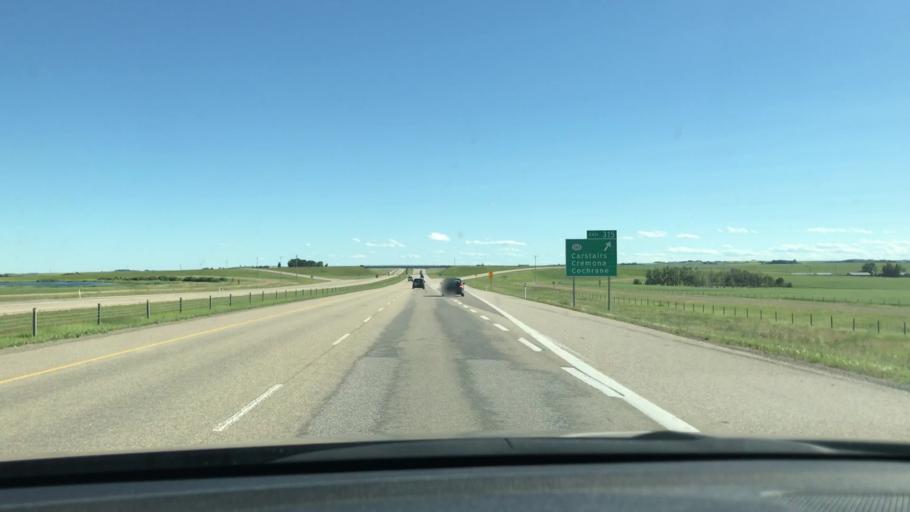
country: CA
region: Alberta
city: Carstairs
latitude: 51.5693
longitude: -114.0255
